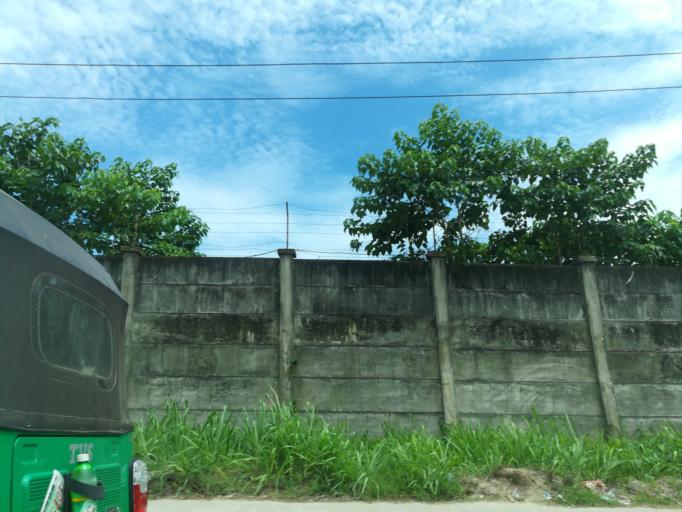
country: NG
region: Lagos
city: Ebute Ikorodu
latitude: 6.5752
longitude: 3.4873
